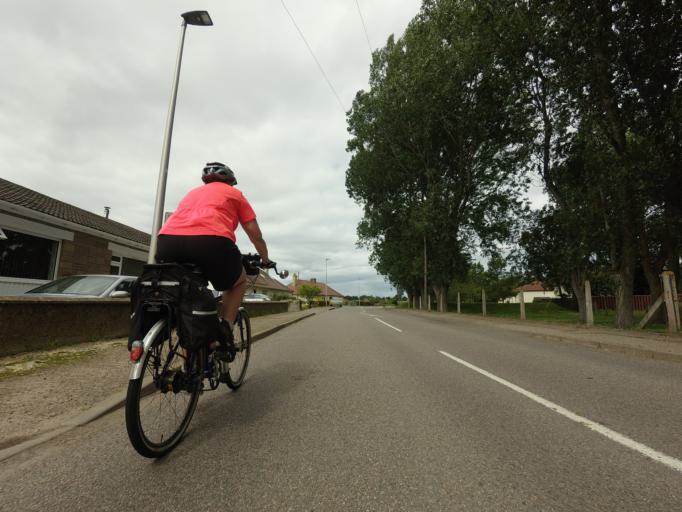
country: GB
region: Scotland
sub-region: Moray
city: Kinloss
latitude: 57.6320
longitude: -3.5597
